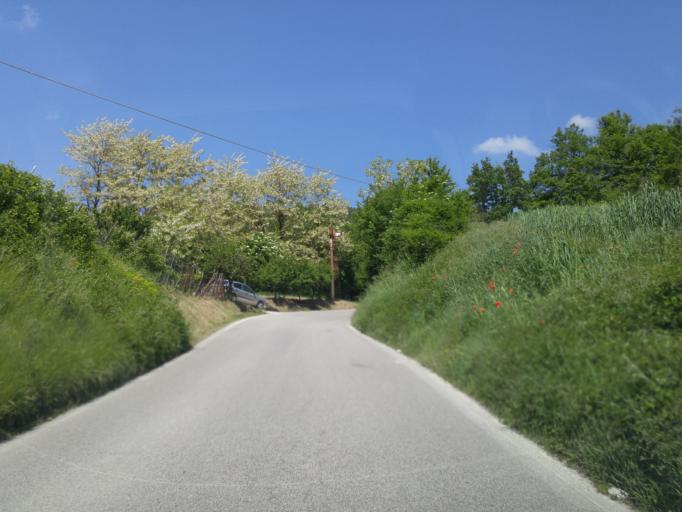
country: IT
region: The Marches
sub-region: Provincia di Pesaro e Urbino
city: Fermignano
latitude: 43.6930
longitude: 12.6413
